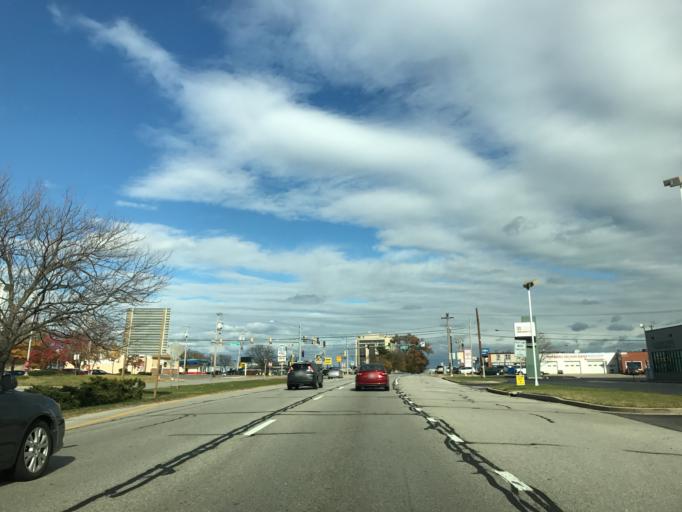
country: US
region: Maryland
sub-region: Anne Arundel County
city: Glen Burnie
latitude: 39.1665
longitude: -76.6222
